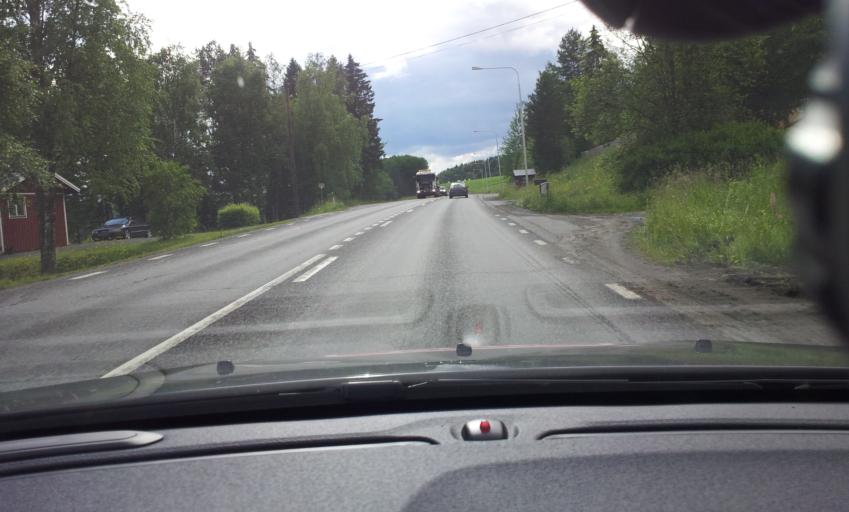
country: SE
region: Jaemtland
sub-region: Are Kommun
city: Jarpen
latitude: 63.3356
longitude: 13.4254
